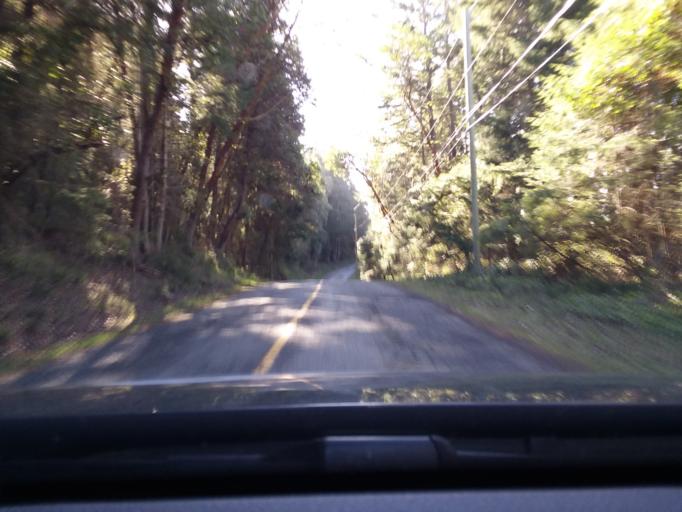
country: CA
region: British Columbia
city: North Cowichan
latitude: 48.9611
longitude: -123.5466
